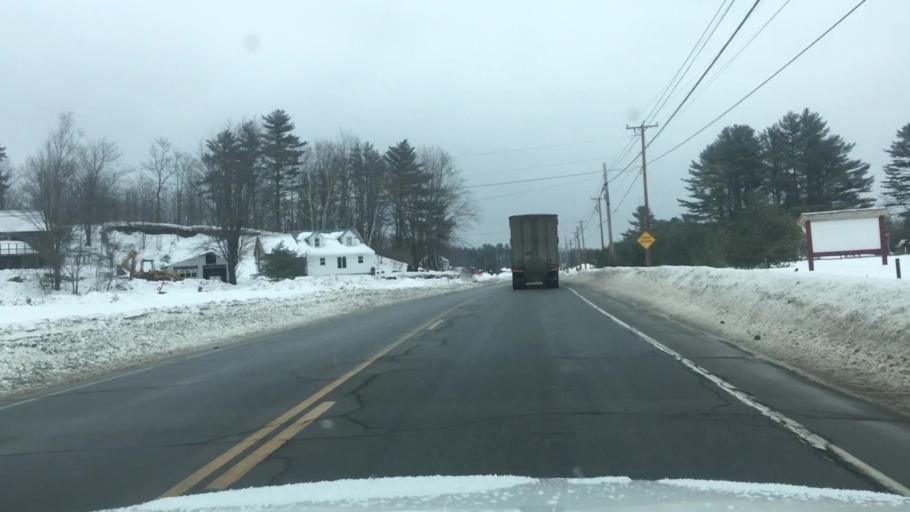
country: US
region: Maine
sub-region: Oxford County
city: Peru
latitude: 44.5186
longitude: -70.4164
